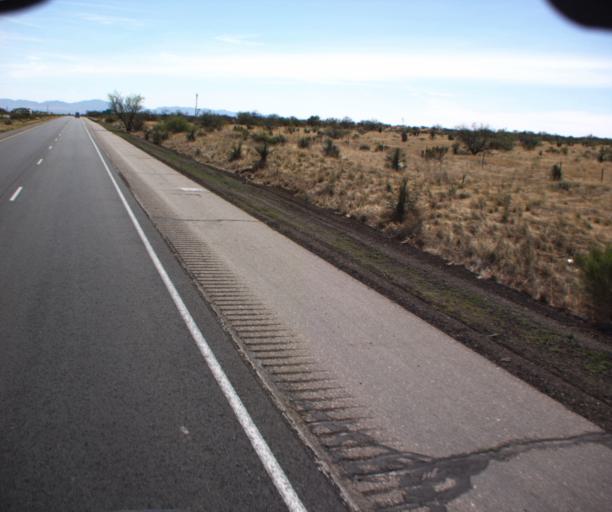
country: US
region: Arizona
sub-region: Cochise County
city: Mescal
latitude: 31.9629
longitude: -110.4140
